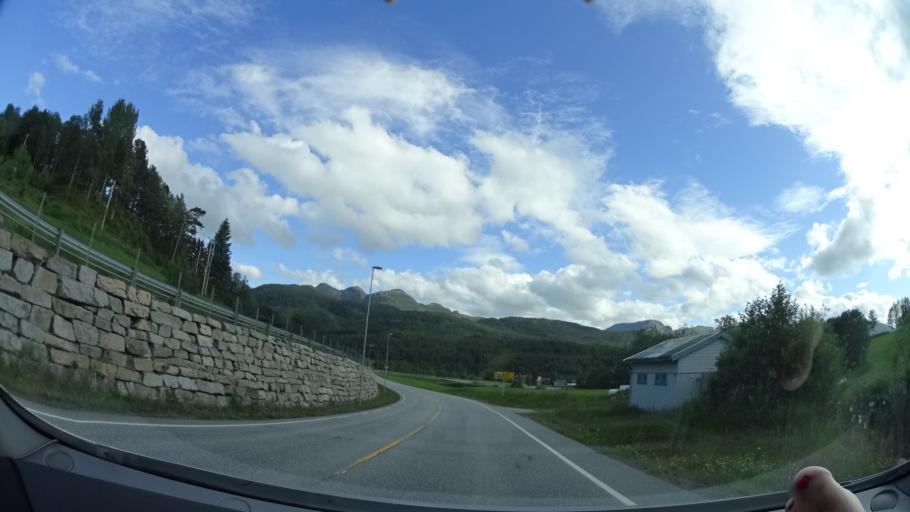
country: NO
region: More og Romsdal
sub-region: Halsa
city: Liaboen
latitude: 63.0926
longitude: 8.3532
